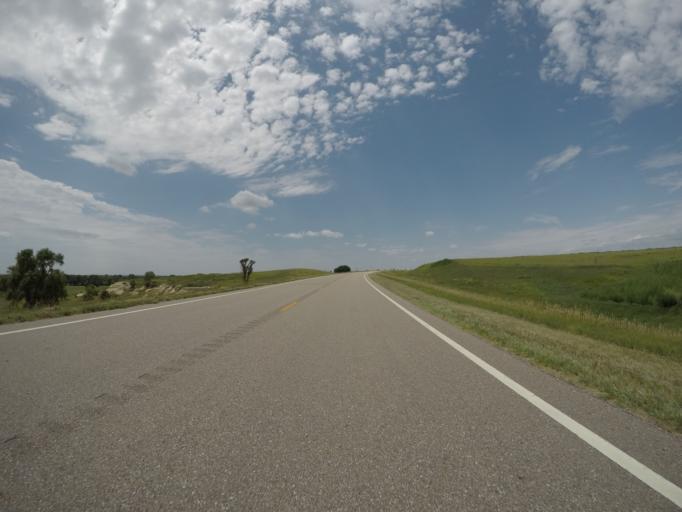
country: US
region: Kansas
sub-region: Graham County
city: Hill City
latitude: 39.3818
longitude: -99.6634
